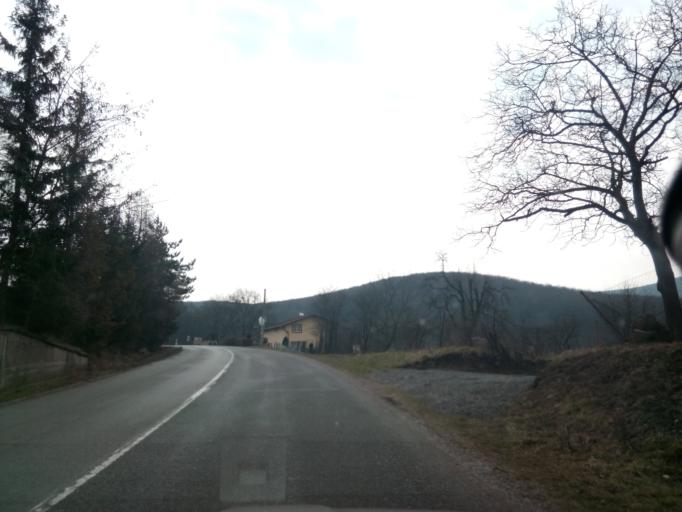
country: SK
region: Kosicky
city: Kosice
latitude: 48.6436
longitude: 21.4288
